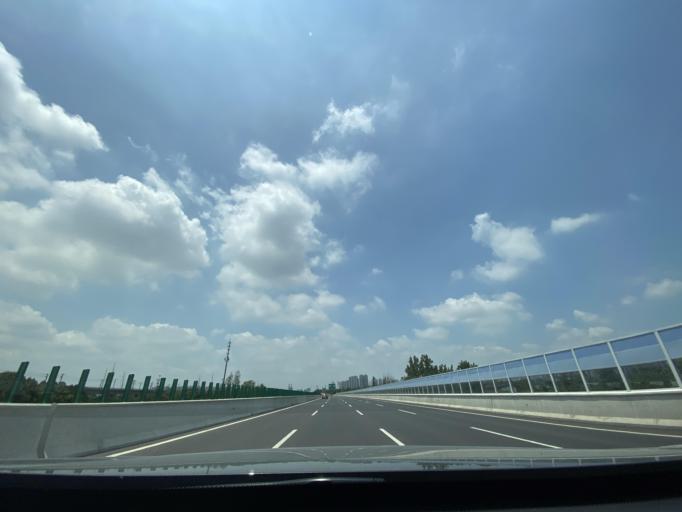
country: CN
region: Sichuan
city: Chengdu
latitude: 30.5802
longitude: 104.1330
